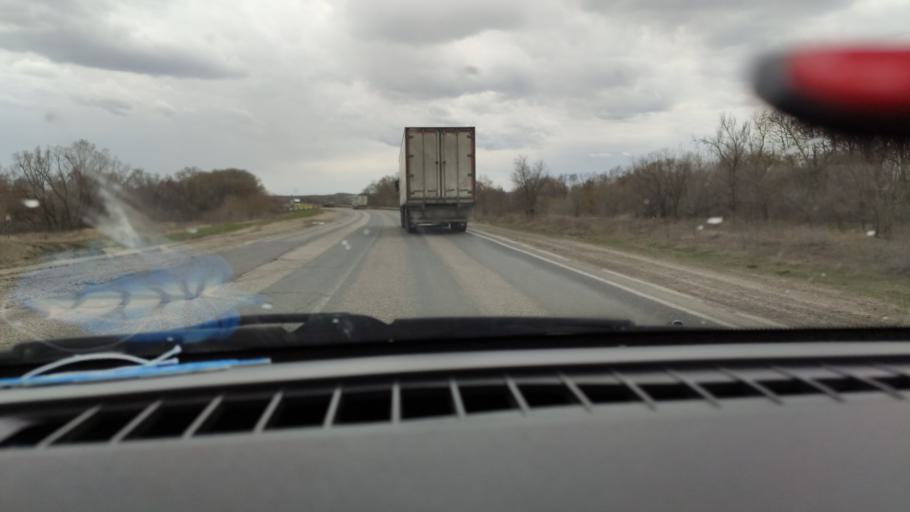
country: RU
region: Saratov
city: Sinodskoye
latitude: 51.9744
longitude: 46.6463
